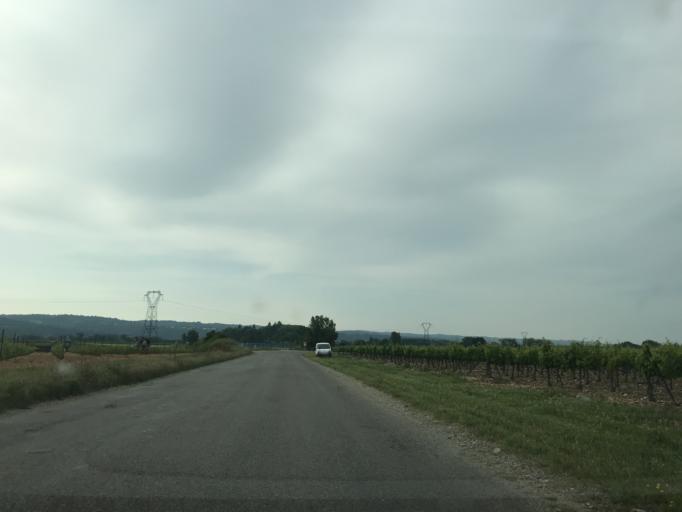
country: FR
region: Provence-Alpes-Cote d'Azur
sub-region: Departement des Alpes-de-Haute-Provence
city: Volx
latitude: 43.8466
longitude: 5.8328
